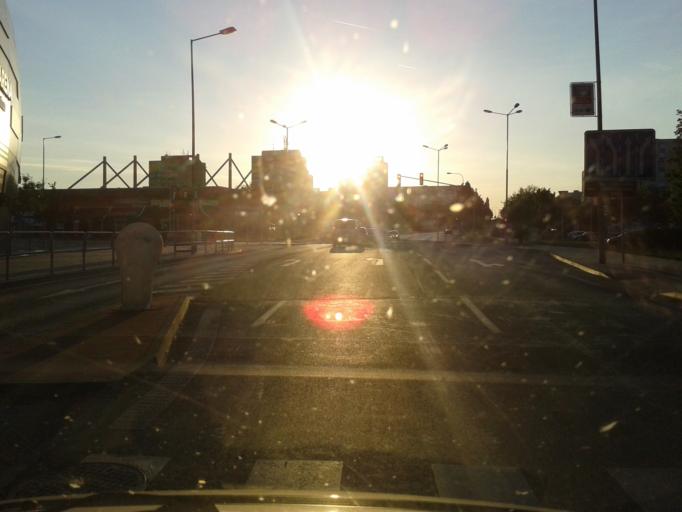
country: SK
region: Trnavsky
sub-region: Okres Trnava
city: Trnava
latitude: 48.3731
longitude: 17.5929
